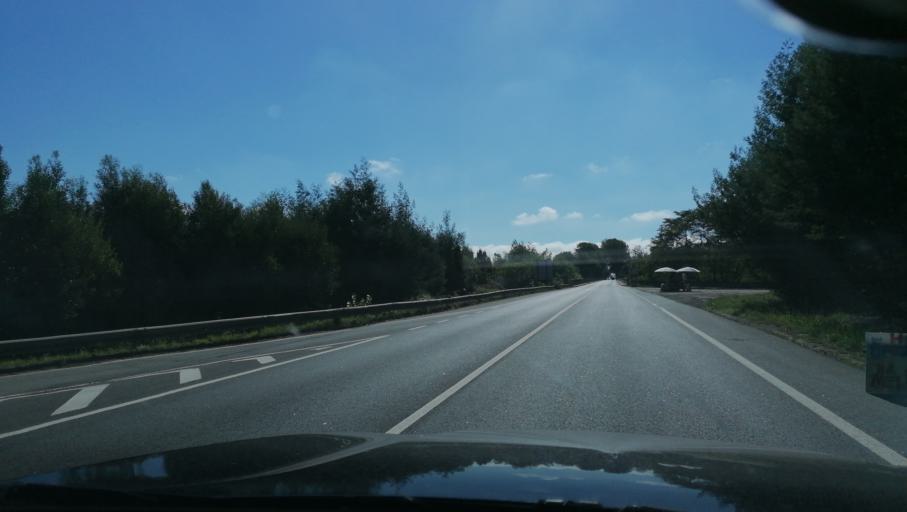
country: PT
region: Aveiro
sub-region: Aveiro
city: Eixo
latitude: 40.6819
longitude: -8.5790
